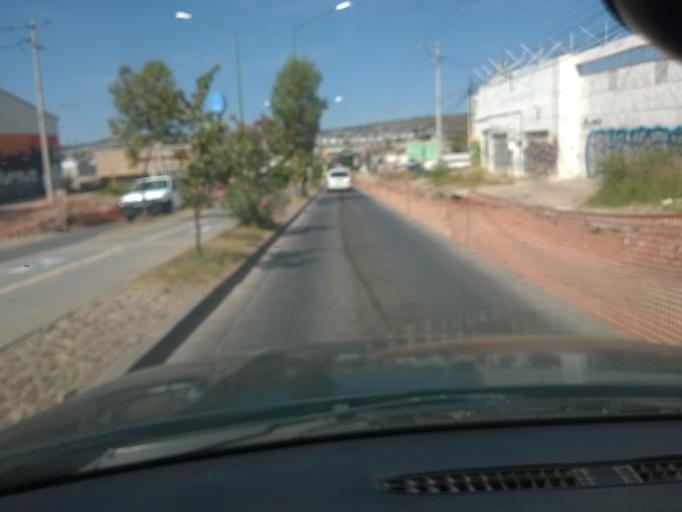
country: MX
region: Guanajuato
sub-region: Leon
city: Ejido la Joya
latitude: 21.1394
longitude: -101.7346
